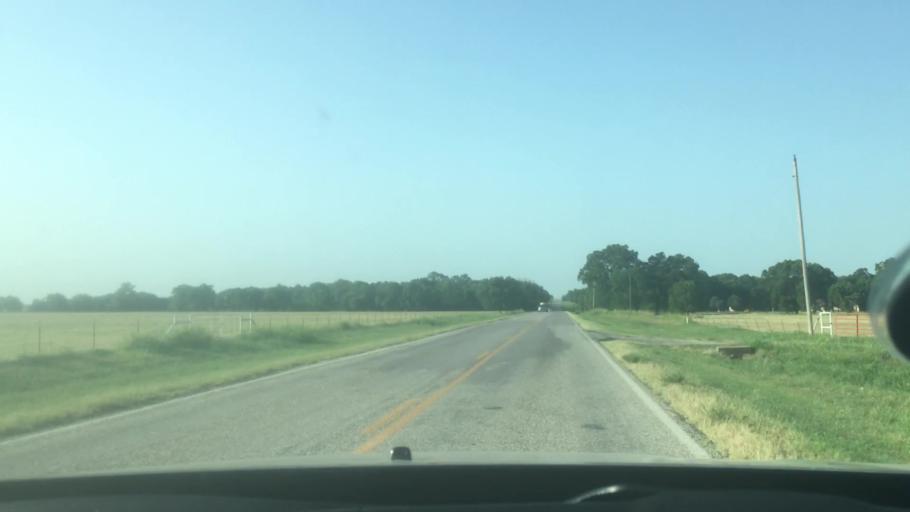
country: US
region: Oklahoma
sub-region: Johnston County
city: Tishomingo
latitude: 34.3029
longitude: -96.4248
